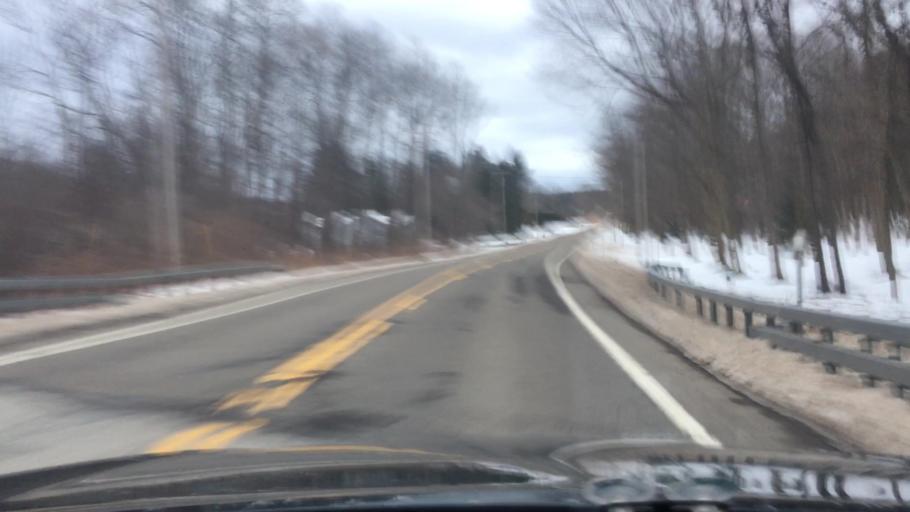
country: US
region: New York
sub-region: Chautauqua County
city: Lakewood
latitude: 42.1731
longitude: -79.3745
